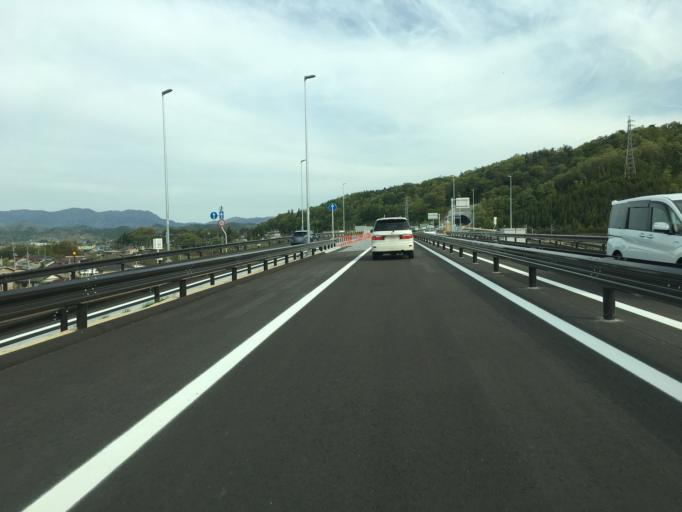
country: JP
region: Fukushima
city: Hobaramachi
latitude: 37.8117
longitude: 140.5365
